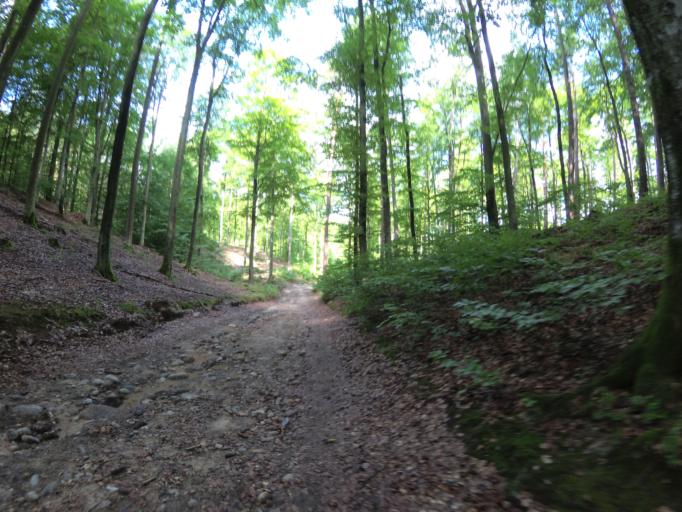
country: PL
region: Pomeranian Voivodeship
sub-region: Gdynia
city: Wielki Kack
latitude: 54.5076
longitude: 18.4566
